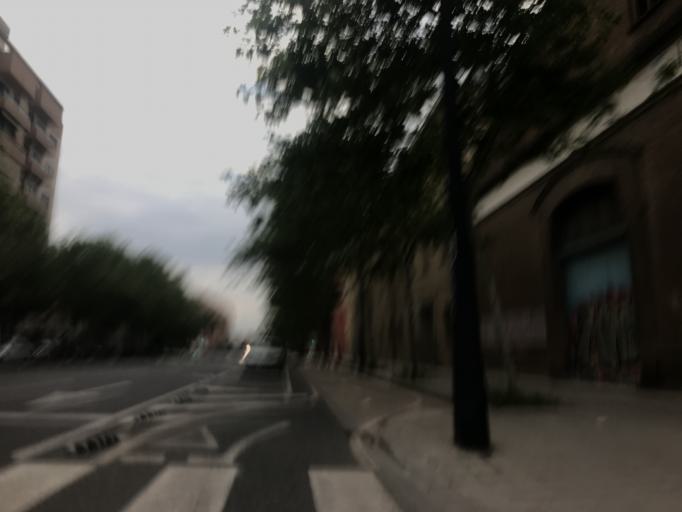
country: ES
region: Valencia
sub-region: Provincia de Valencia
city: Valencia
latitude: 39.4587
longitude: -0.3373
